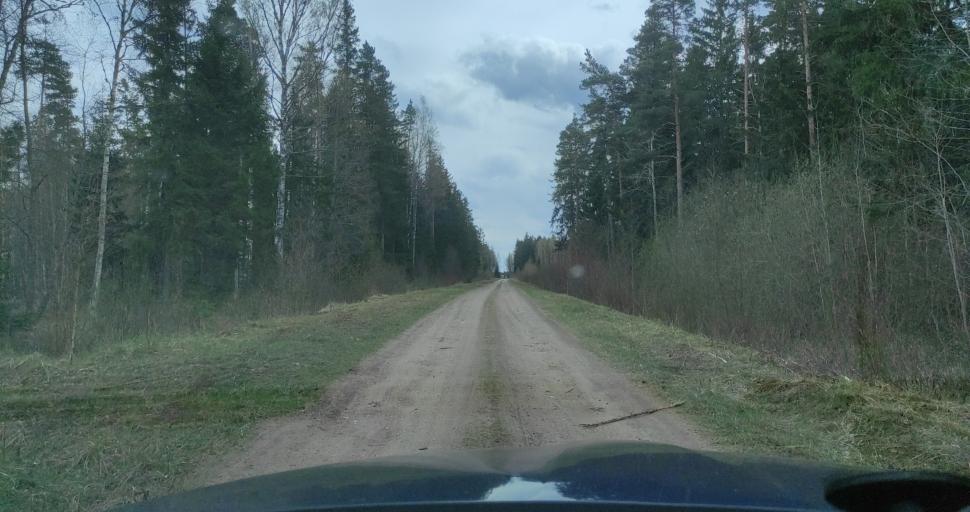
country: LV
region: Dundaga
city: Dundaga
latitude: 57.3613
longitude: 22.1509
